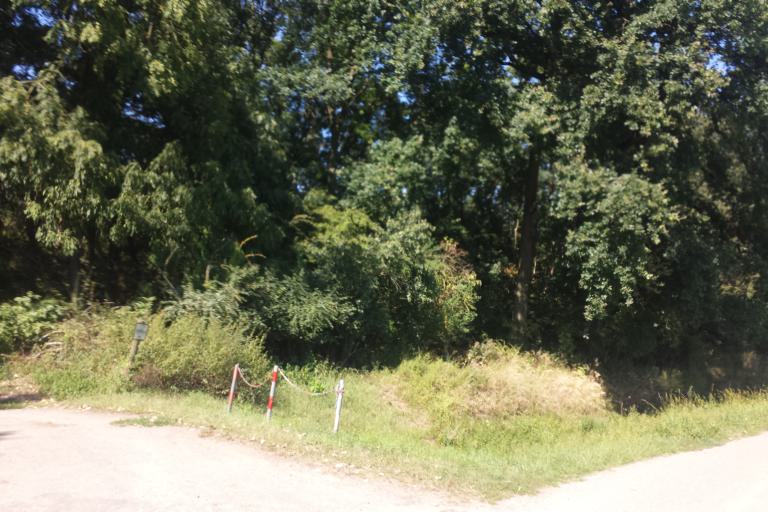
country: DE
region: Hesse
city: Viernheim
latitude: 49.5766
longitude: 8.5953
